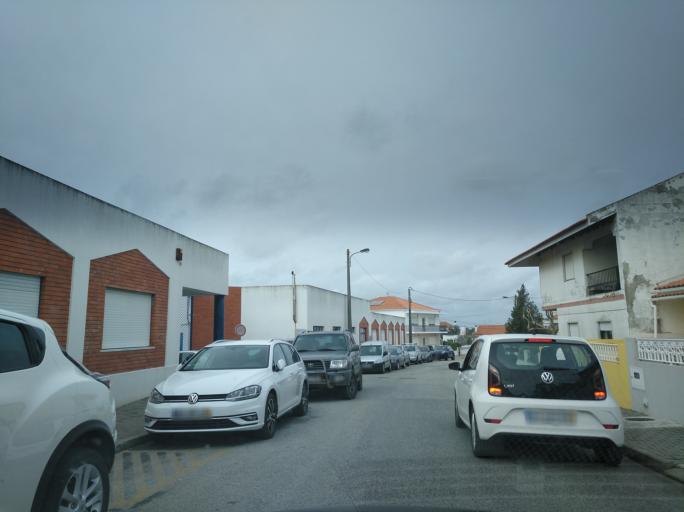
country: PT
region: Setubal
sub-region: Grandola
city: Grandola
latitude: 38.1771
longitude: -8.5695
